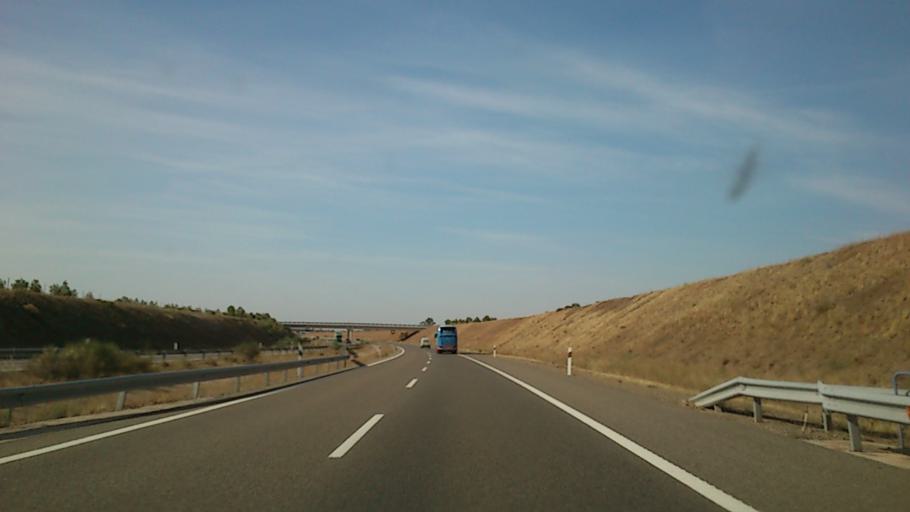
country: ES
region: Aragon
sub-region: Provincia de Zaragoza
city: Carinena
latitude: 41.3312
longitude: -1.2031
